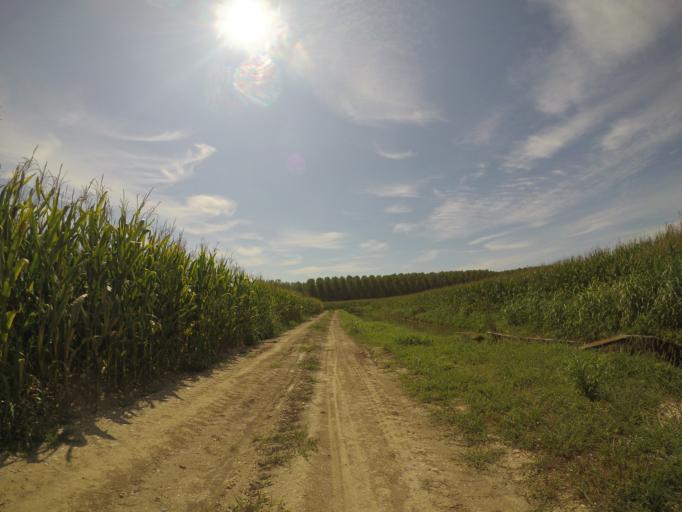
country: IT
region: Friuli Venezia Giulia
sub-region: Provincia di Udine
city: Varmo
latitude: 45.9184
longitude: 13.0184
